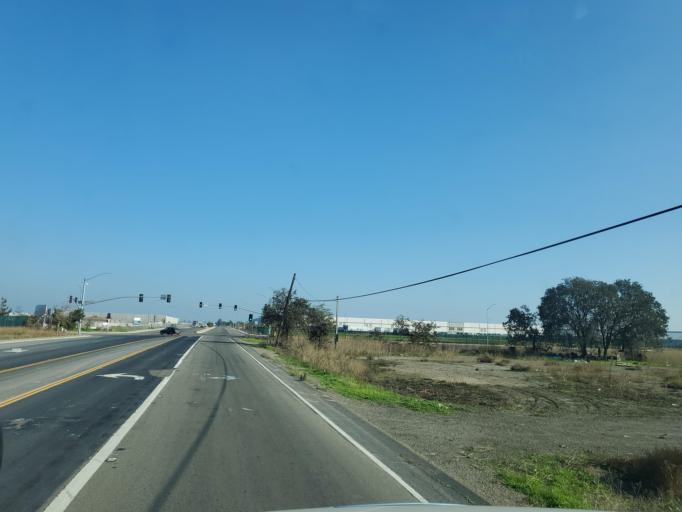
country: US
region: California
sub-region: San Joaquin County
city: Kennedy
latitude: 37.9053
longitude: -121.2035
